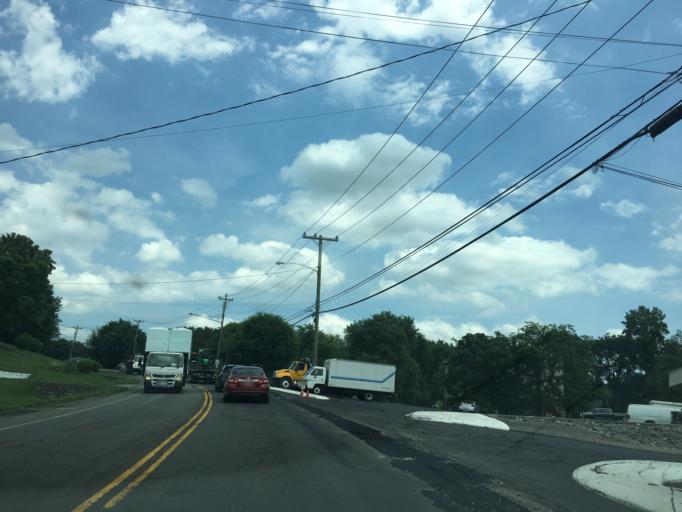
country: US
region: Tennessee
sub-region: Davidson County
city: Nashville
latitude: 36.1301
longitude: -86.7528
